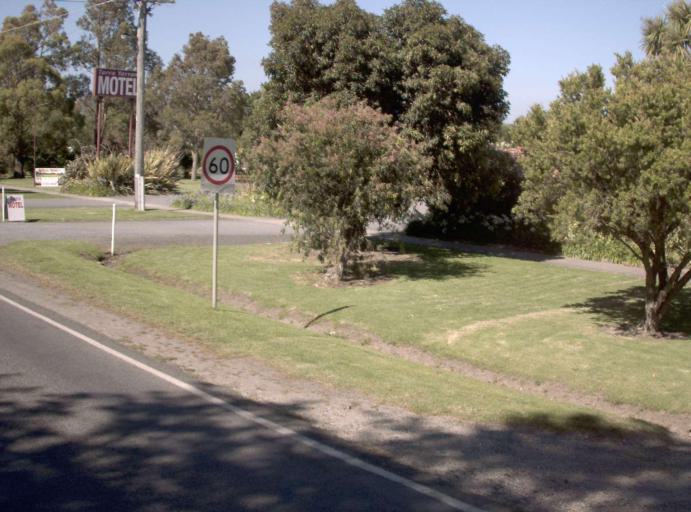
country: AU
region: Victoria
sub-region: Latrobe
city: Traralgon
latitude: -38.5705
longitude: 146.6744
